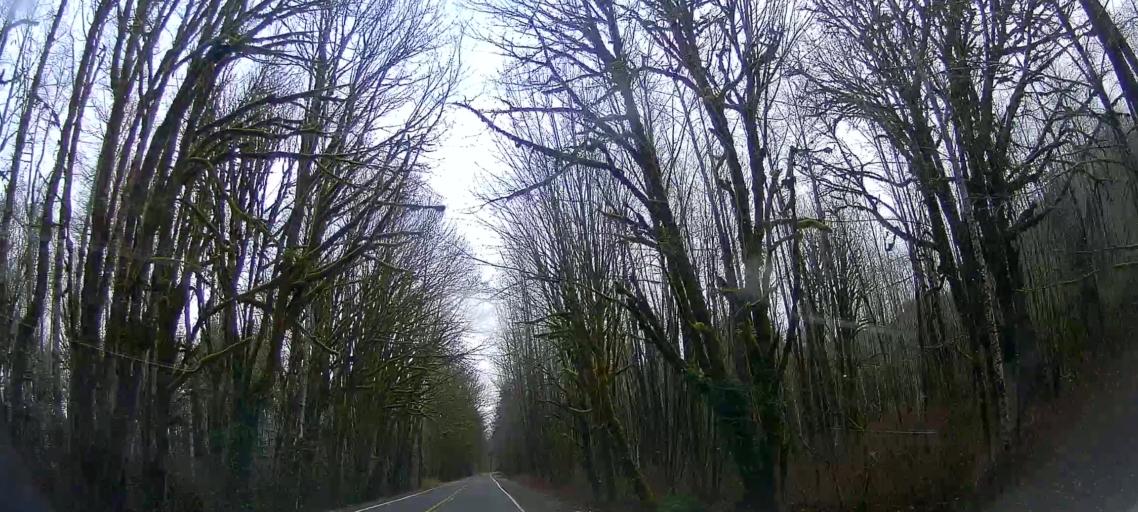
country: US
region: Washington
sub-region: Skagit County
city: Sedro-Woolley
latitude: 48.5110
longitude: -121.9166
